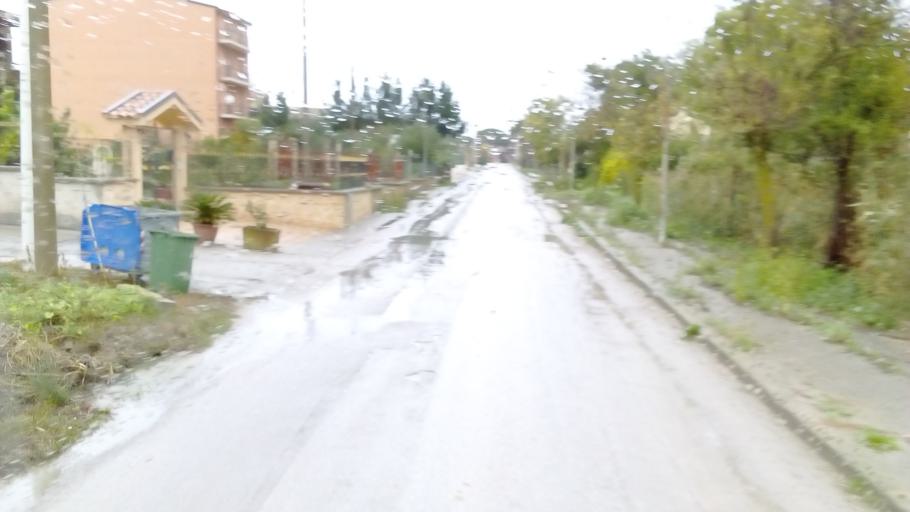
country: IT
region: Sicily
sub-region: Enna
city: Pietraperzia
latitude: 37.4121
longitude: 14.1421
